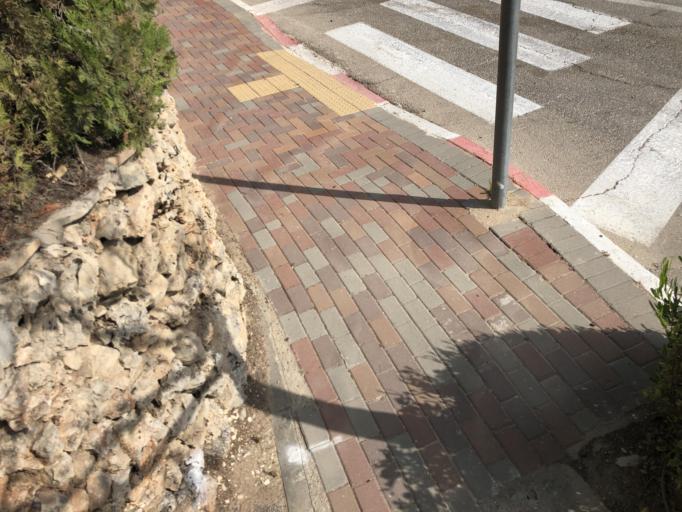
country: PS
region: West Bank
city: Jit
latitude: 32.2126
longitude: 35.1573
